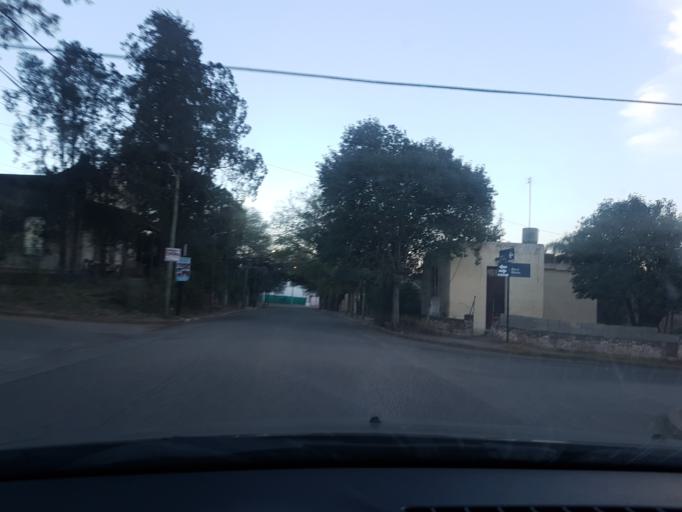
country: AR
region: Cordoba
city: Villa Allende
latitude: -31.2895
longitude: -64.2975
